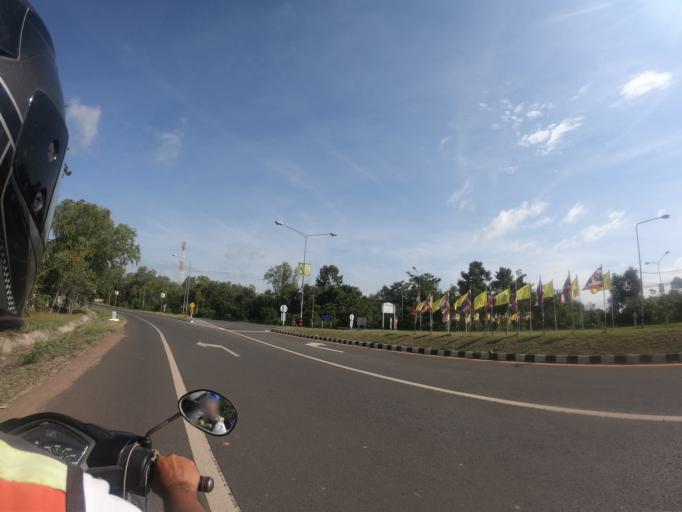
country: TH
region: Surin
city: Kap Choeng
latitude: 14.4509
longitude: 103.6987
